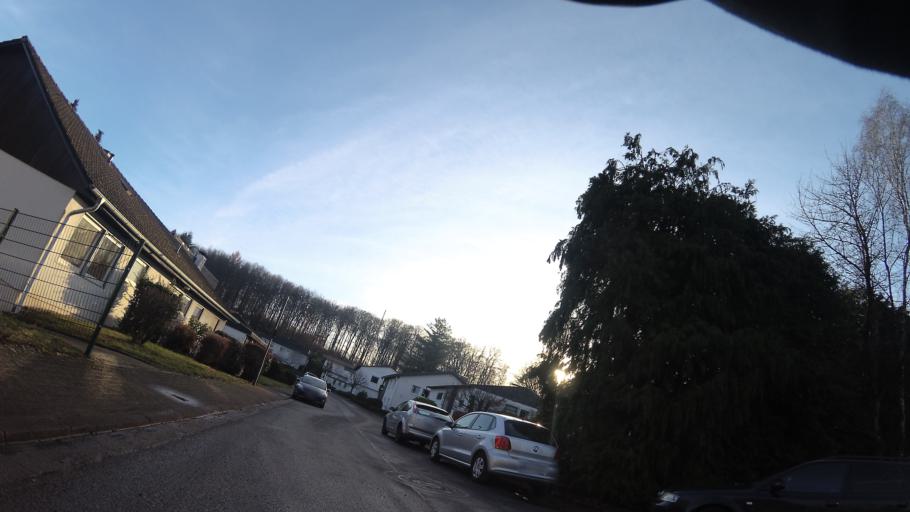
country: DE
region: Saarland
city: Neunkirchen
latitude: 49.3302
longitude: 7.1626
